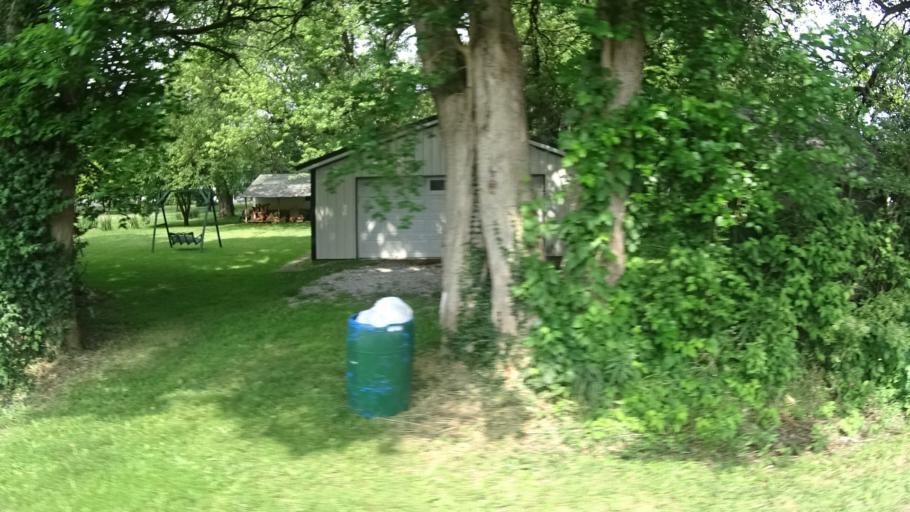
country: US
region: Ohio
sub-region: Lorain County
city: Vermilion
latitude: 41.4000
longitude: -82.4192
